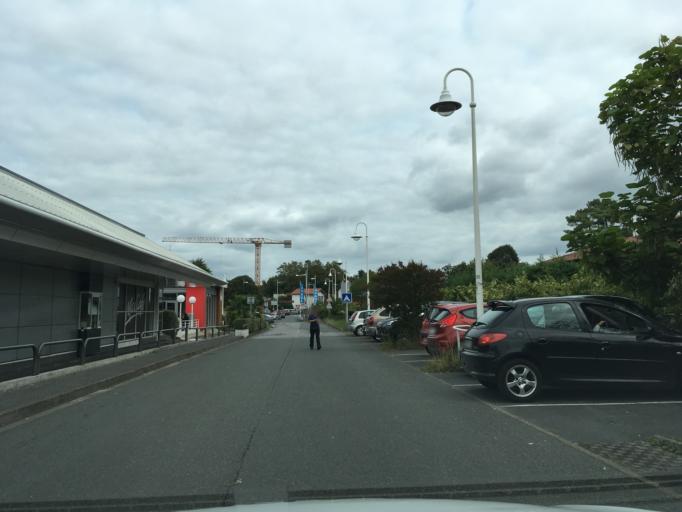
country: FR
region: Aquitaine
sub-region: Departement des Pyrenees-Atlantiques
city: Anglet
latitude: 43.4824
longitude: -1.5035
